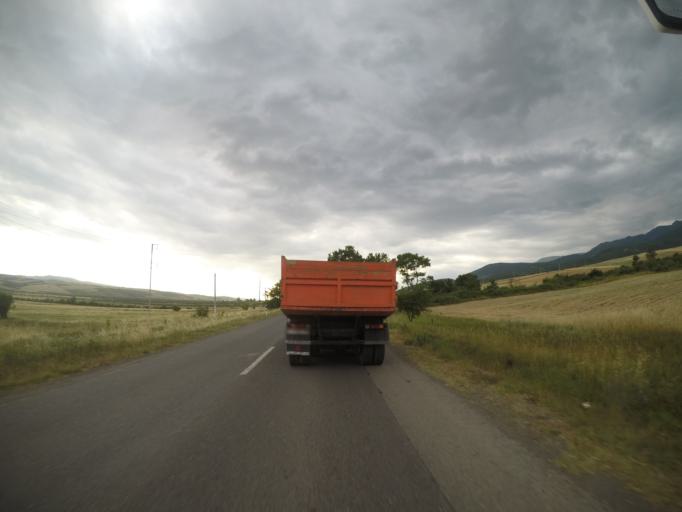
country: AZ
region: Ismayilli
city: Ismayilli
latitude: 40.7437
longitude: 48.2525
